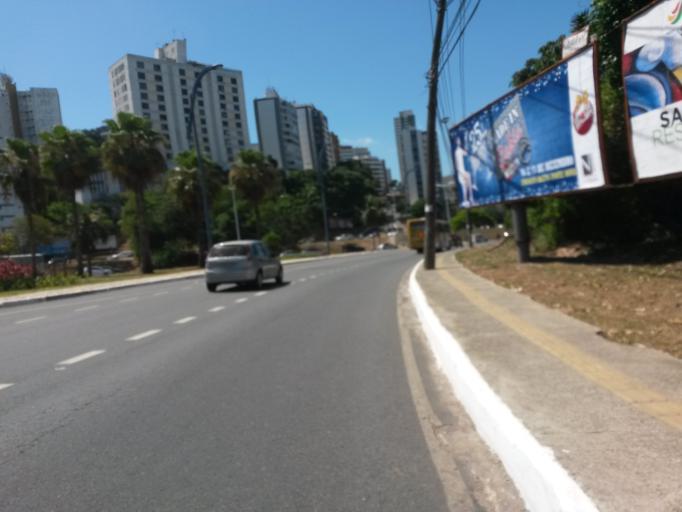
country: BR
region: Bahia
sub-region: Salvador
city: Salvador
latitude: -12.9952
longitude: -38.4747
